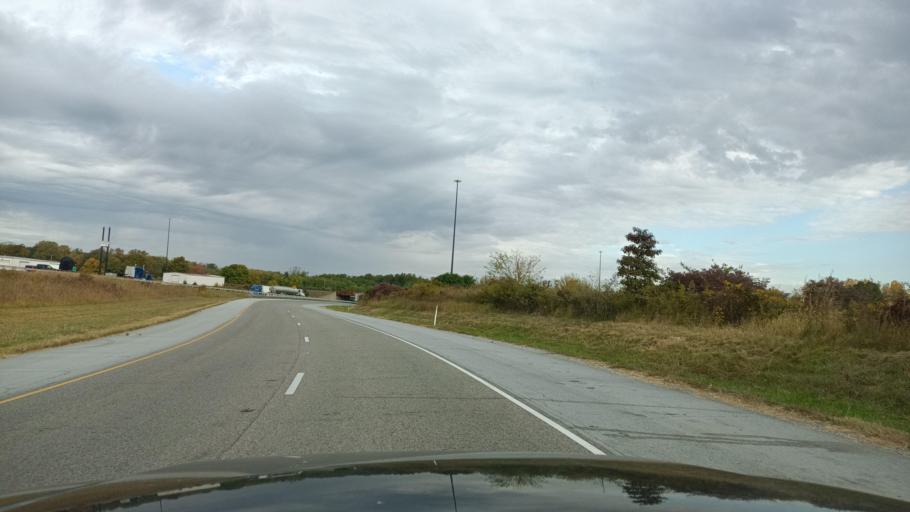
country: US
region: Indiana
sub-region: Delaware County
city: Daleville
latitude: 40.1150
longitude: -85.5674
